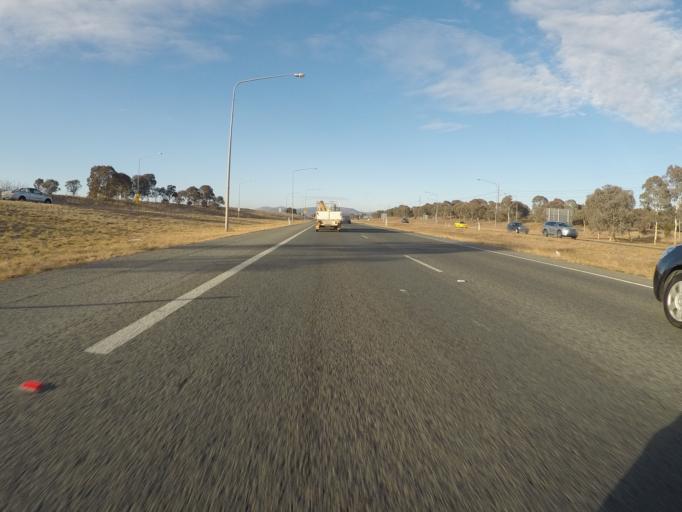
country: AU
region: Australian Capital Territory
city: Forrest
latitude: -35.3421
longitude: 149.1632
